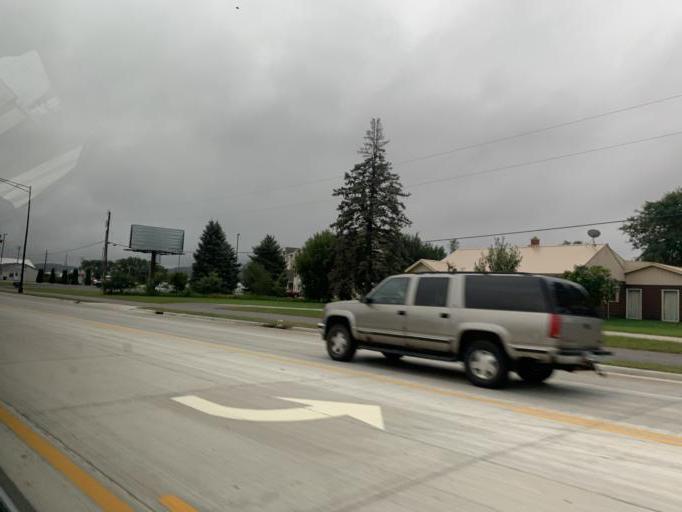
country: US
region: Wisconsin
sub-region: Crawford County
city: Prairie du Chien
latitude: 43.0309
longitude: -91.1315
